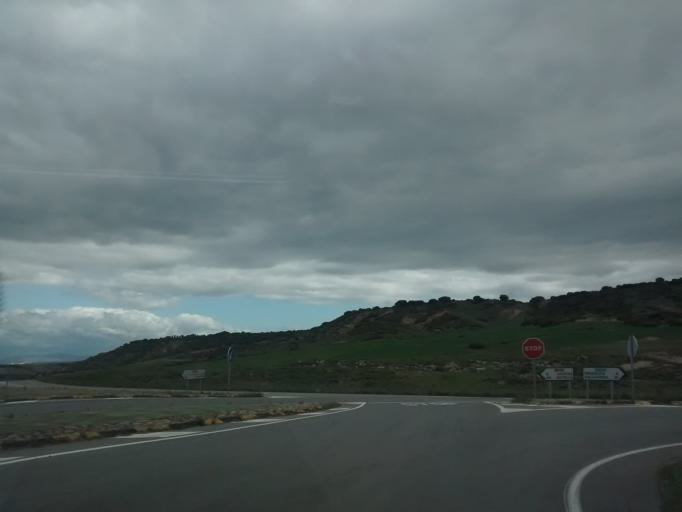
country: ES
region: La Rioja
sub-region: Provincia de La Rioja
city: Pradejon
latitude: 42.3454
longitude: -2.0904
